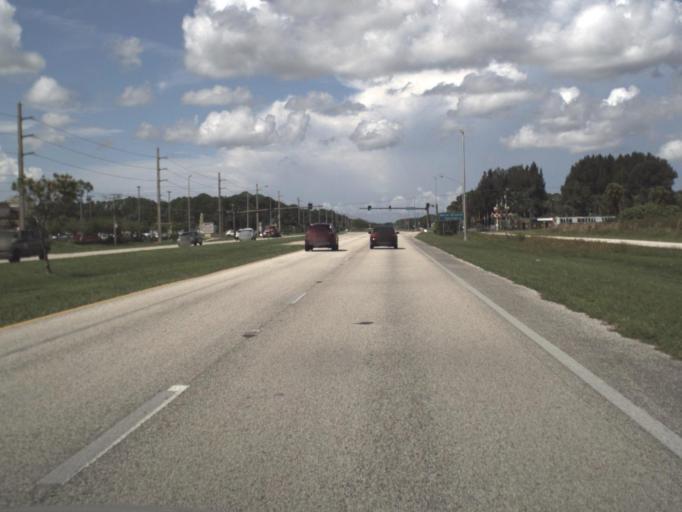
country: US
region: Florida
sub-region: Sarasota County
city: Warm Mineral Springs
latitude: 27.0468
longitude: -82.2588
